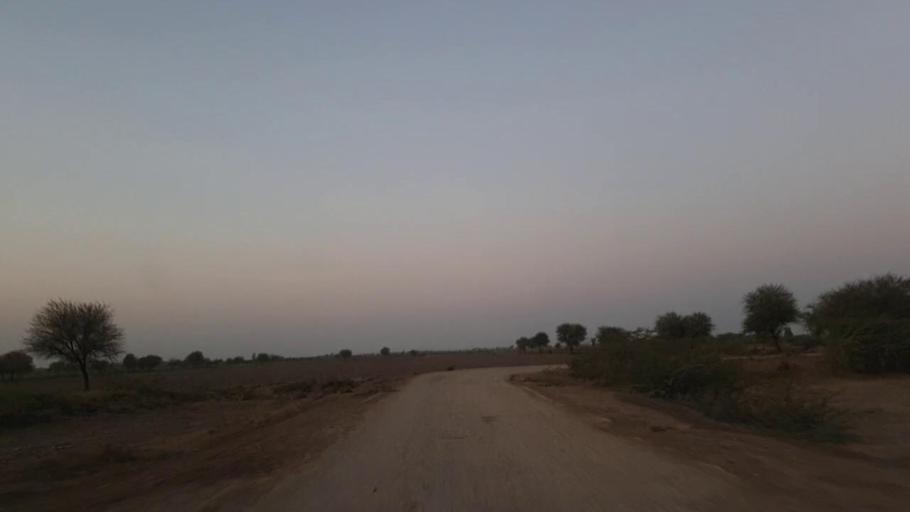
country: PK
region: Sindh
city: Naukot
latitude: 24.8758
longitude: 69.3898
